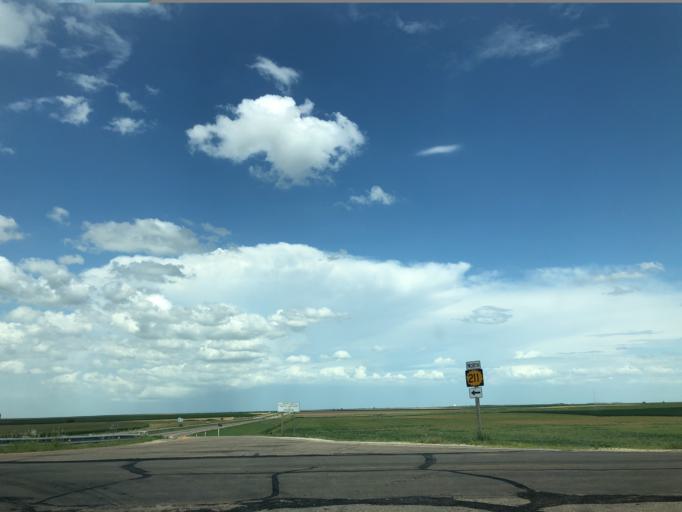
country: US
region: Kansas
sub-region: Gove County
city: Gove
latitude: 39.0967
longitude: -100.3702
